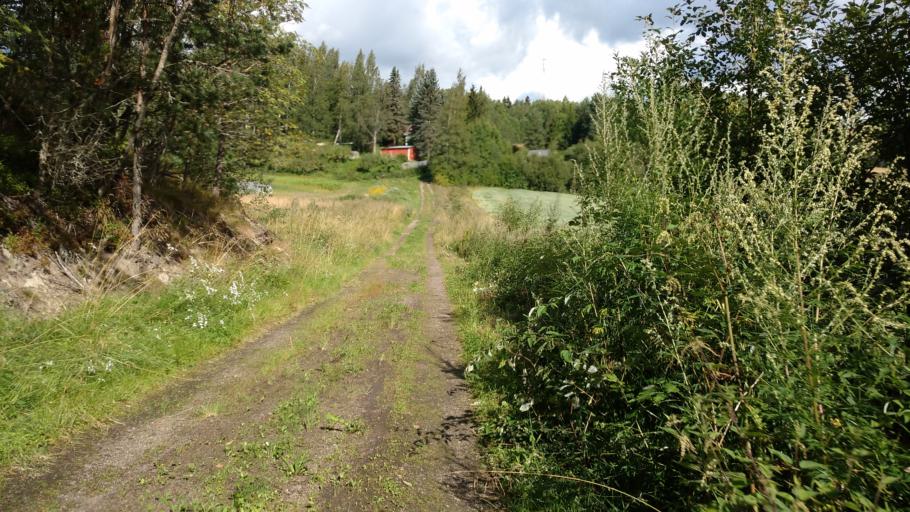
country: FI
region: Varsinais-Suomi
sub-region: Salo
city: Salo
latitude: 60.3520
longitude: 23.1362
